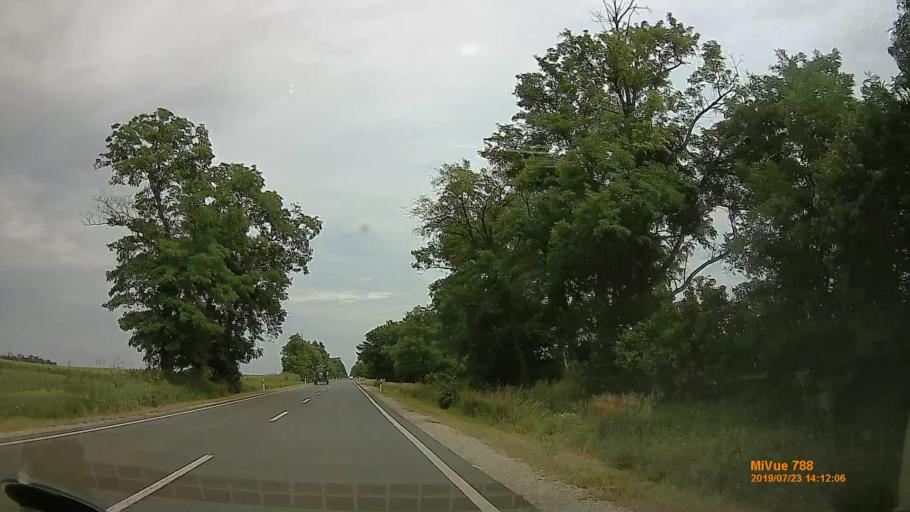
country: HU
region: Szabolcs-Szatmar-Bereg
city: Tiszalok
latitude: 47.9593
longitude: 21.4469
